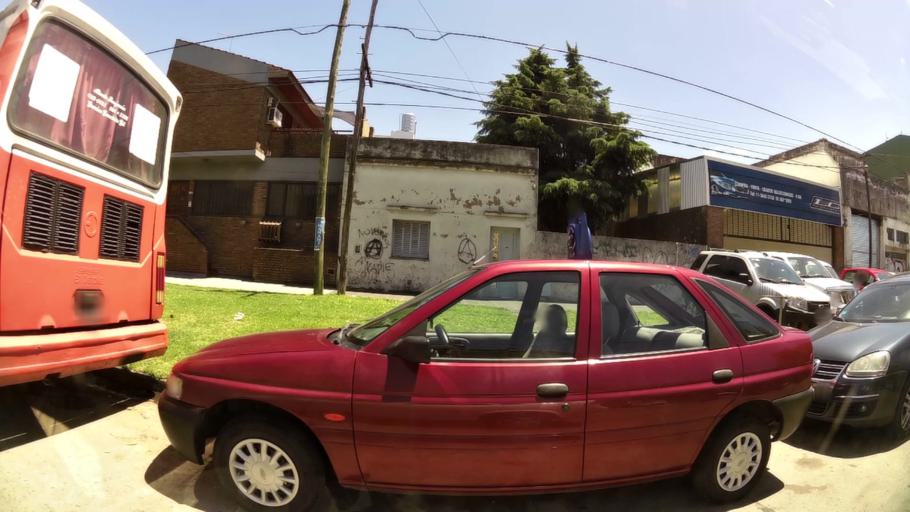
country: AR
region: Buenos Aires
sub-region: Partido de General San Martin
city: General San Martin
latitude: -34.5672
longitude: -58.5155
